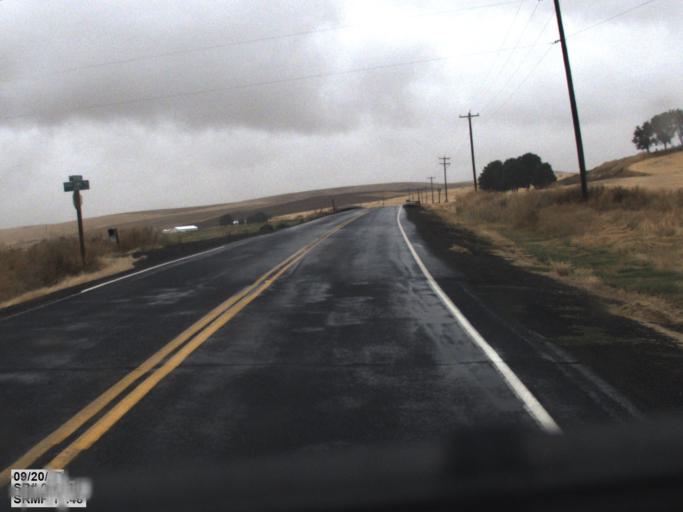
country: US
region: Washington
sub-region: Whitman County
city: Colfax
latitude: 47.0737
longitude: -117.5361
